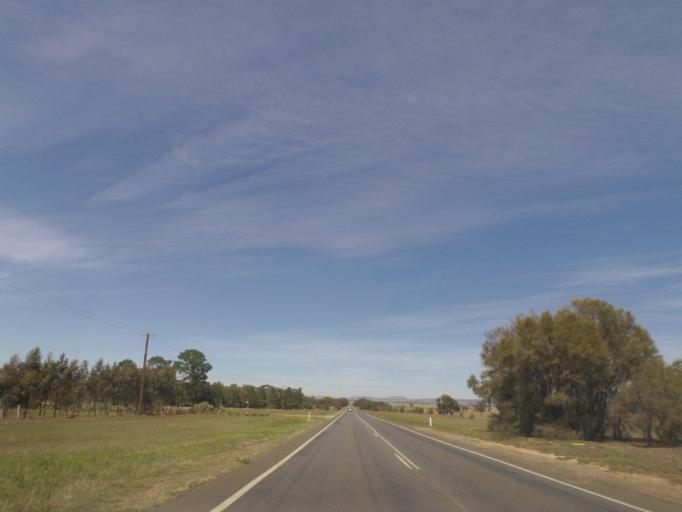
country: AU
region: Victoria
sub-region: Moorabool
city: Bacchus Marsh
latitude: -37.7883
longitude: 144.4222
